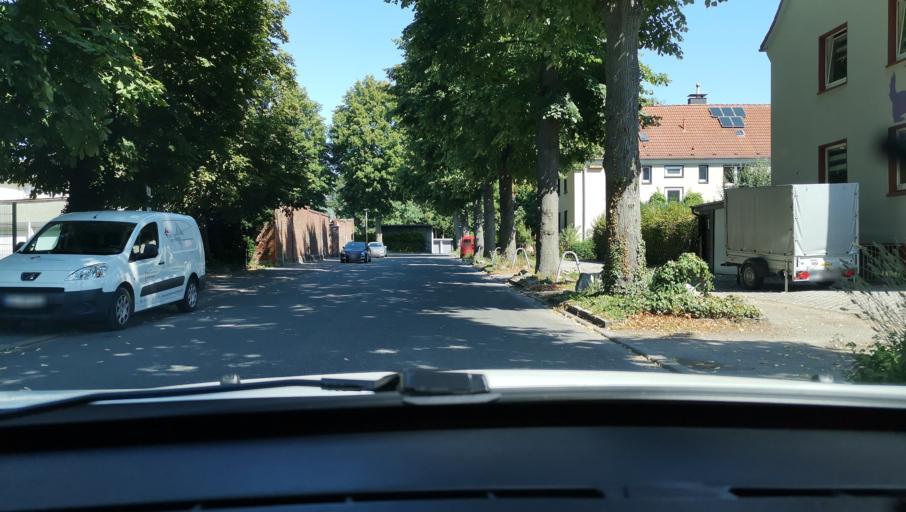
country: DE
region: North Rhine-Westphalia
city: Herdecke
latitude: 51.3830
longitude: 7.4532
